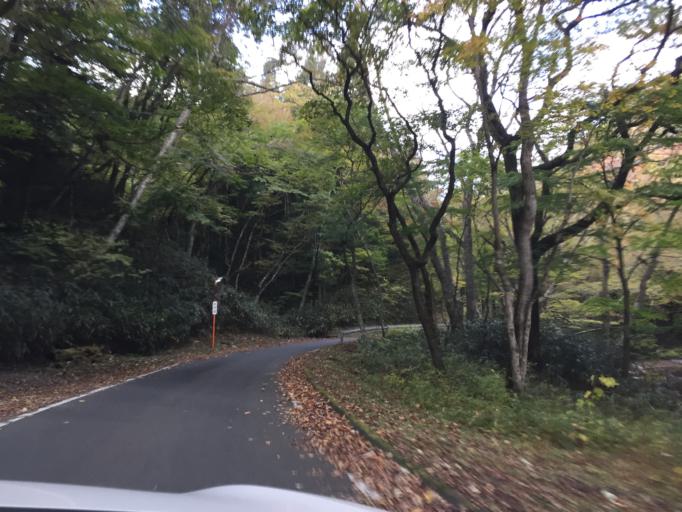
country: JP
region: Fukushima
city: Iwaki
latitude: 37.2126
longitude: 140.7574
